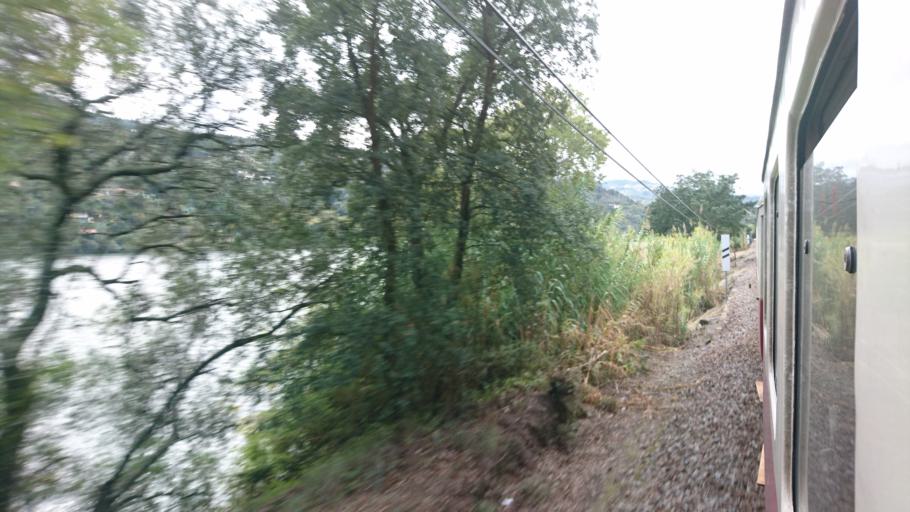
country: PT
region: Viseu
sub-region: Resende
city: Resende
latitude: 41.1097
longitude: -7.9945
